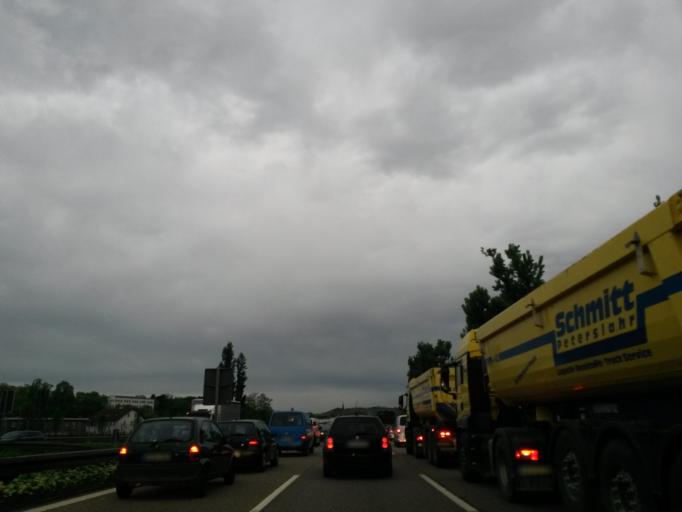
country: DE
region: Baden-Wuerttemberg
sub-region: Regierungsbezirk Stuttgart
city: Stuttgart-Ost
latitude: 48.7900
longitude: 9.2208
